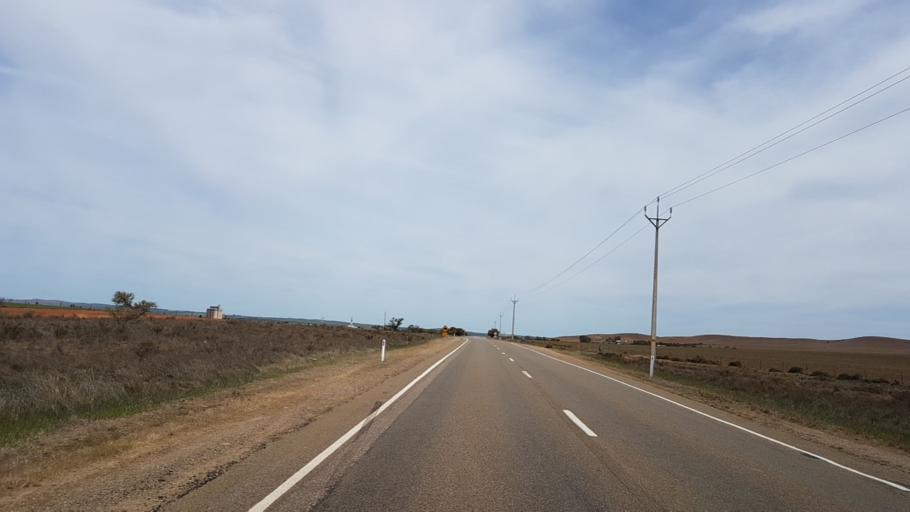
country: AU
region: South Australia
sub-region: Peterborough
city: Peterborough
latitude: -33.0147
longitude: 138.7598
